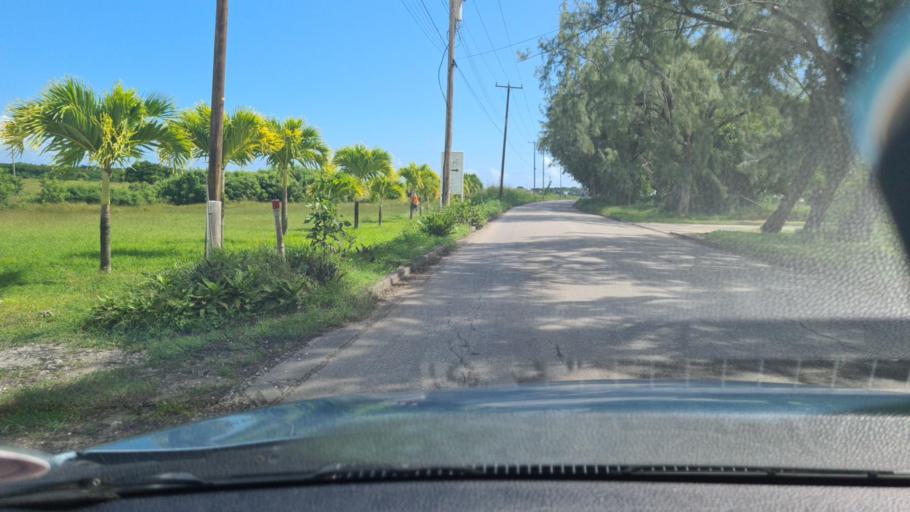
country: BB
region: Saint Philip
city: Crane
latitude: 13.1173
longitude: -59.4703
